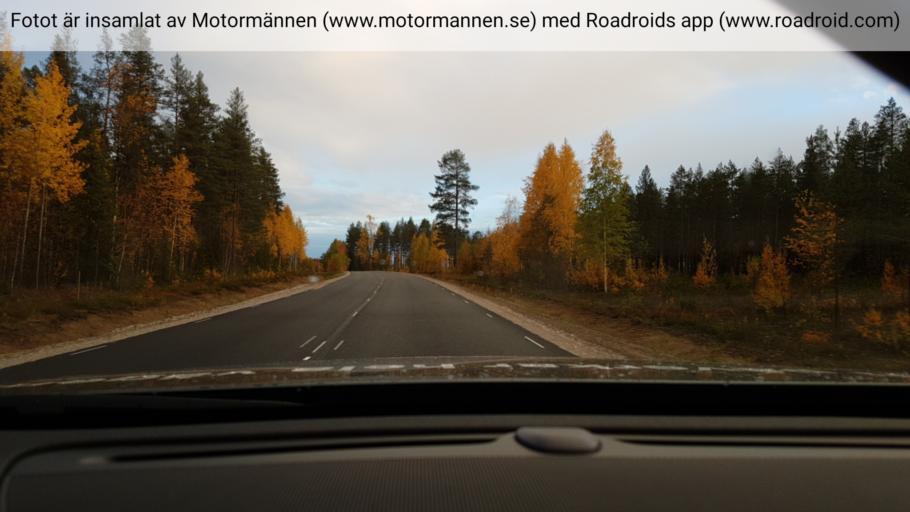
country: SE
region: Norrbotten
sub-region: Overkalix Kommun
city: OEverkalix
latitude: 66.4054
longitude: 22.8064
